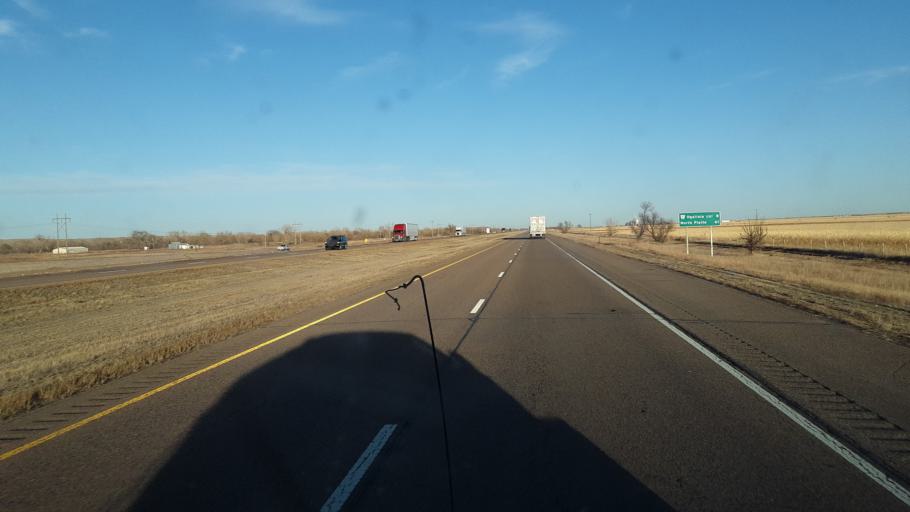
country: US
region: Nebraska
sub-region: Keith County
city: Ogallala
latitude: 41.0823
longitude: -101.8740
